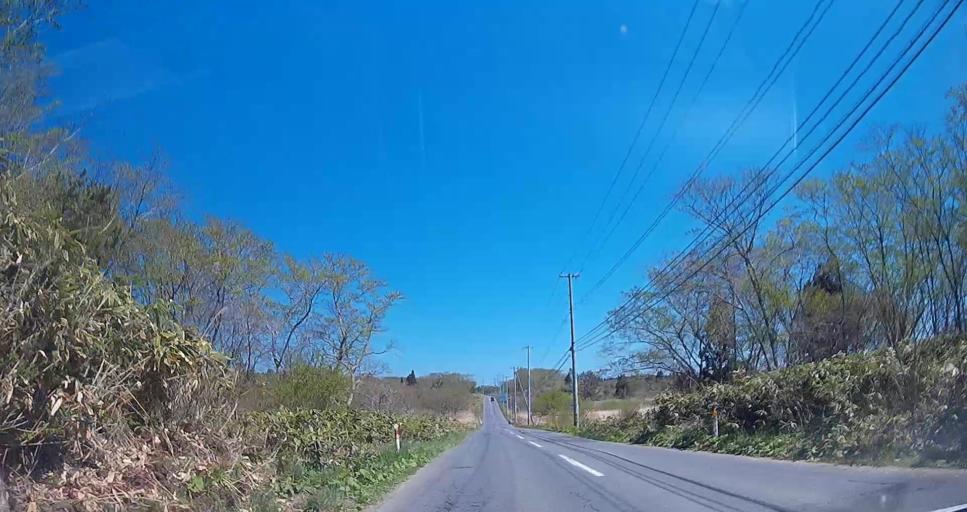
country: JP
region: Aomori
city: Misawa
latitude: 40.9141
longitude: 141.3735
